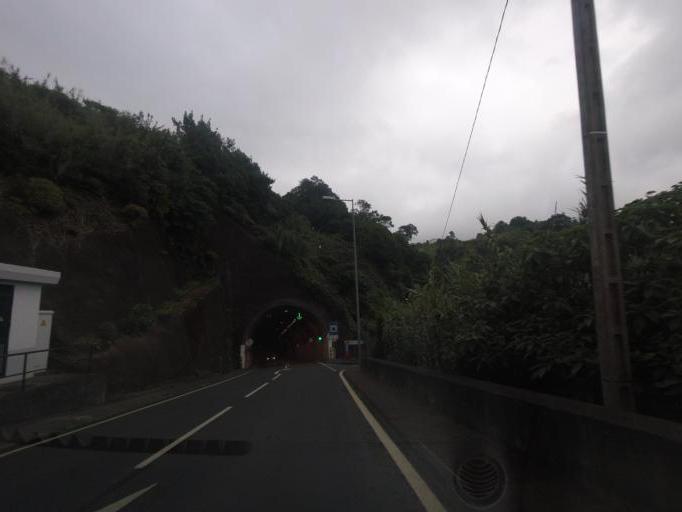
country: PT
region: Madeira
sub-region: Santana
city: Santana
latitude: 32.8190
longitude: -16.8911
